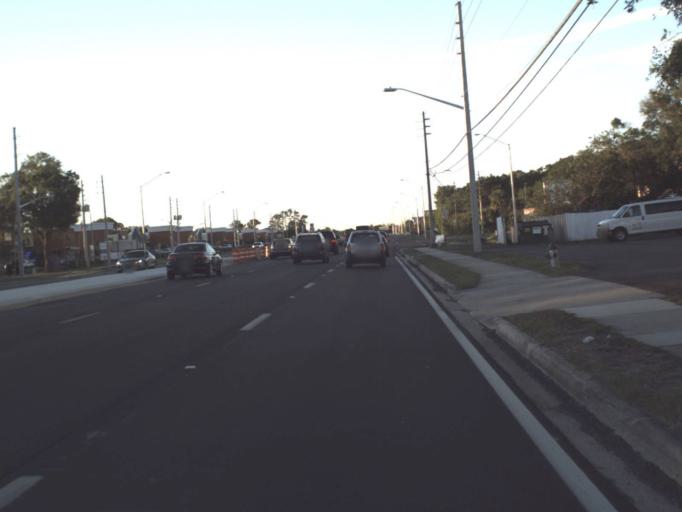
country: US
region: Florida
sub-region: Orange County
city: Azalea Park
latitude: 28.5638
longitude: -81.3108
